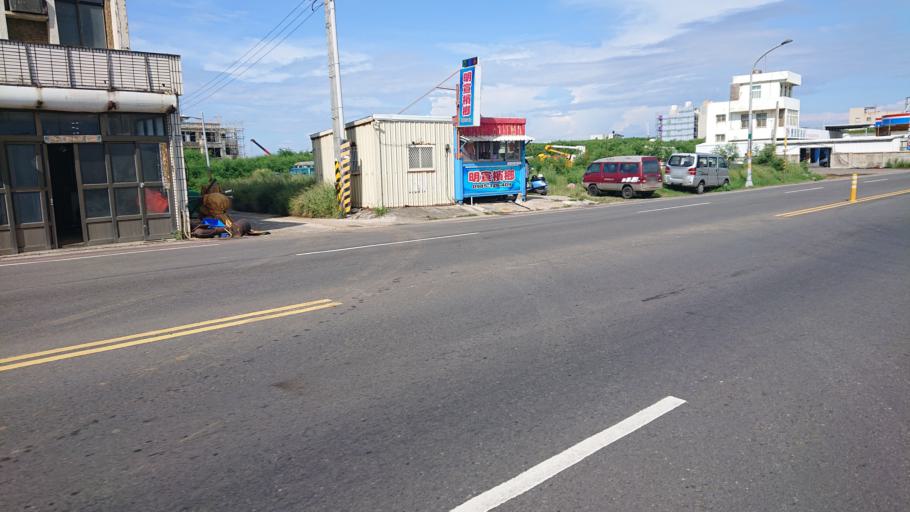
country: TW
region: Taiwan
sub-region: Penghu
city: Ma-kung
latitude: 23.5619
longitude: 119.5931
